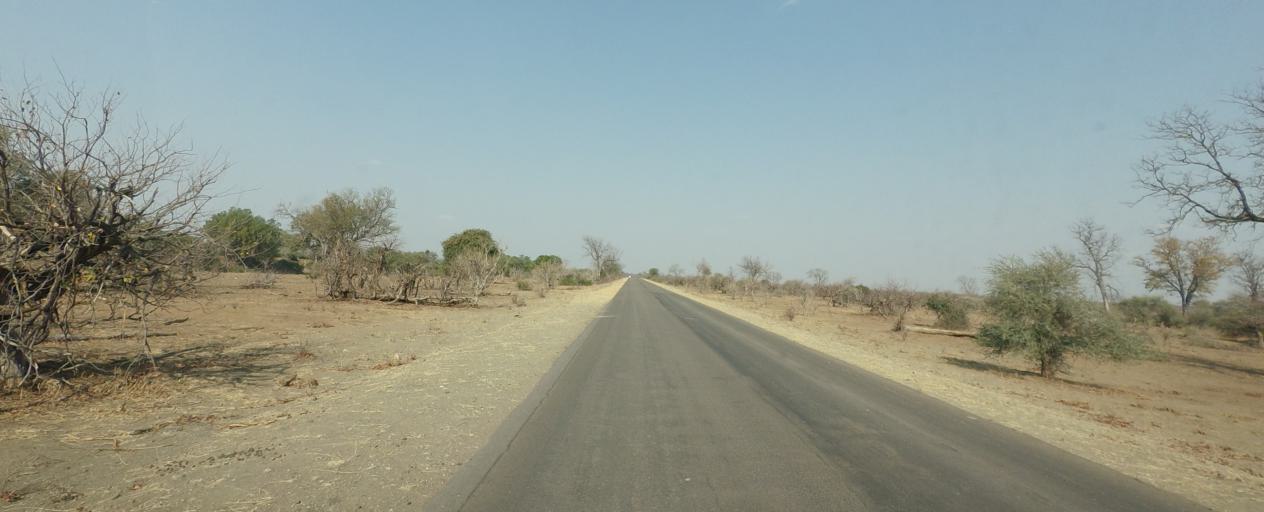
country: ZA
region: Limpopo
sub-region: Mopani District Municipality
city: Giyani
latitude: -23.0972
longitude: 31.3997
